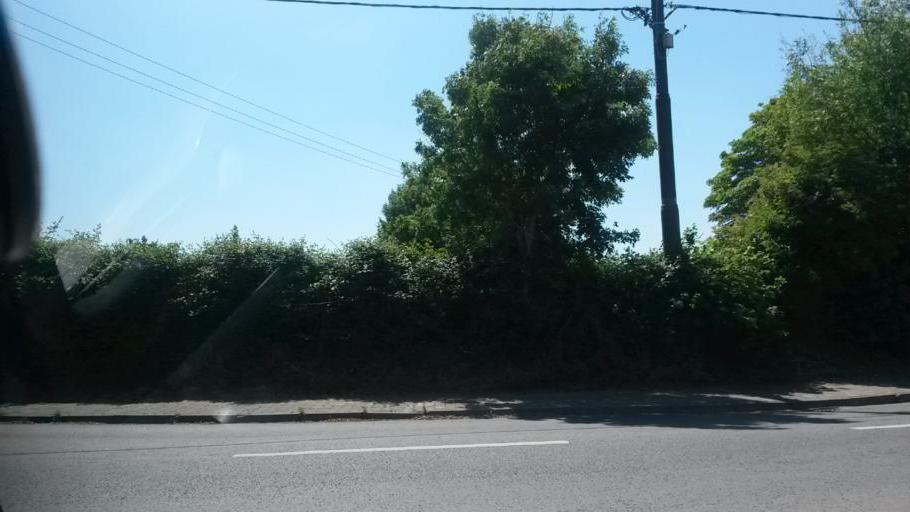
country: IE
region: Leinster
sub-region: An Mhi
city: Ashbourne
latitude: 53.5240
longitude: -6.3151
